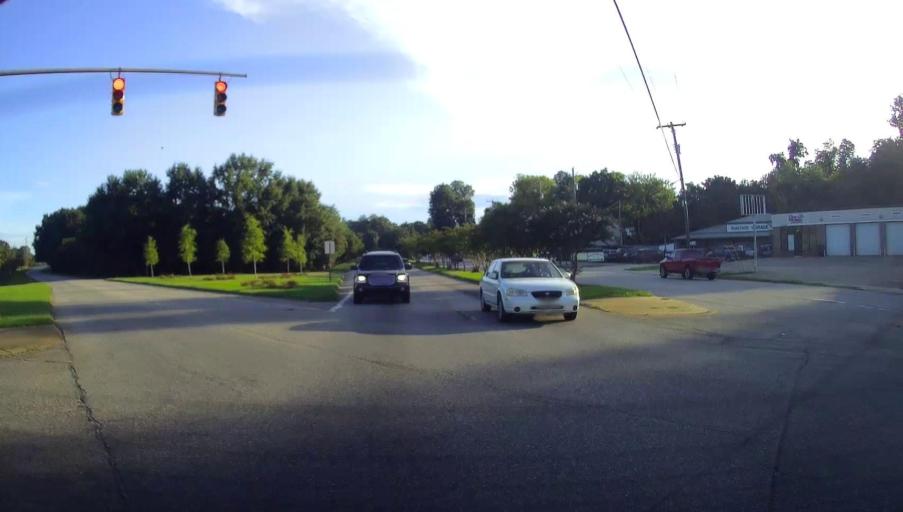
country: US
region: Alabama
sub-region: Russell County
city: Phenix City
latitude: 32.4622
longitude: -85.0008
